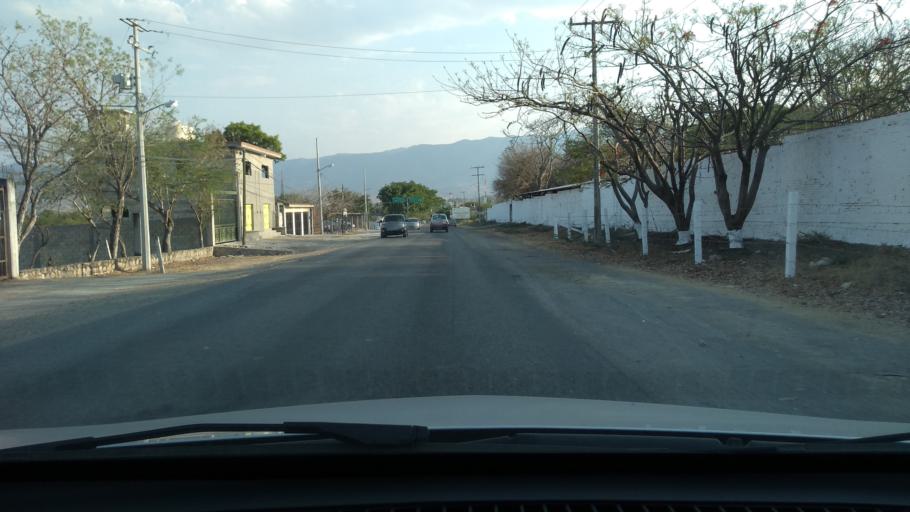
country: MX
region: Morelos
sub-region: Jojutla
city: Tehuixtla
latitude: 18.5683
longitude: -99.2692
